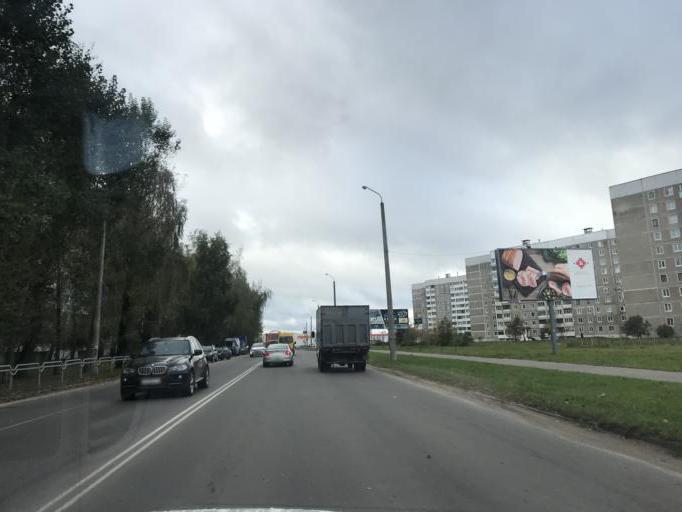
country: BY
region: Mogilev
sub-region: Mahilyowski Rayon
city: Veyno
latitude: 53.8756
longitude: 30.3662
